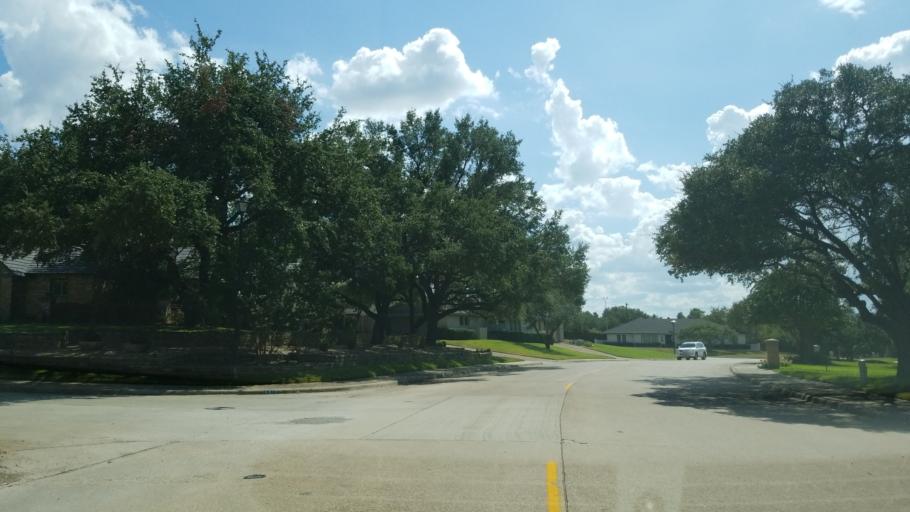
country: US
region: Texas
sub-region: Dallas County
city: Addison
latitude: 32.9517
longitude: -96.7916
